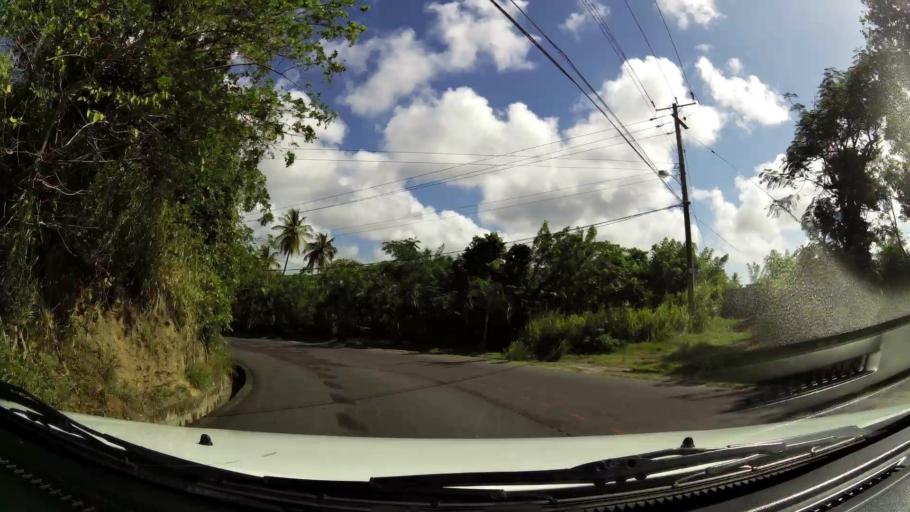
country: LC
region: Choiseul Quarter
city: Choiseul
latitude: 13.7591
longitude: -61.0251
